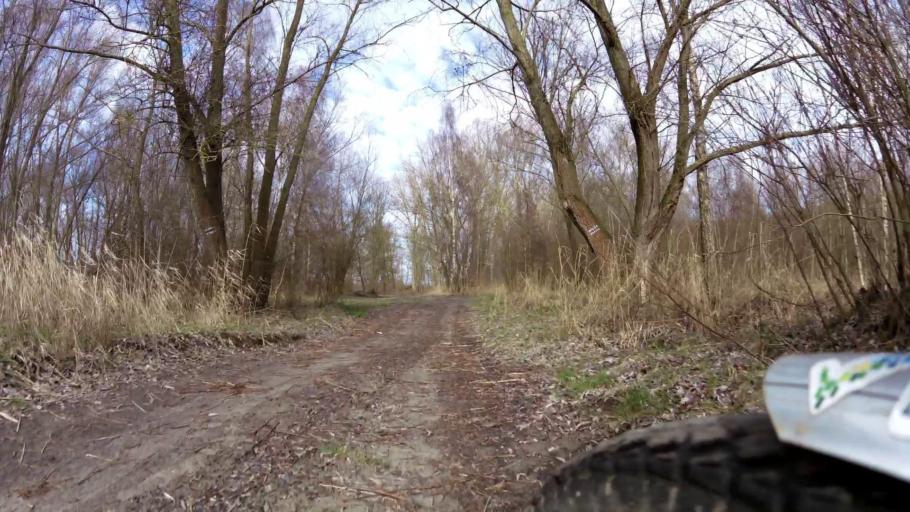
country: PL
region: West Pomeranian Voivodeship
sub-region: Powiat kamienski
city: Kamien Pomorski
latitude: 53.9803
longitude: 14.7692
